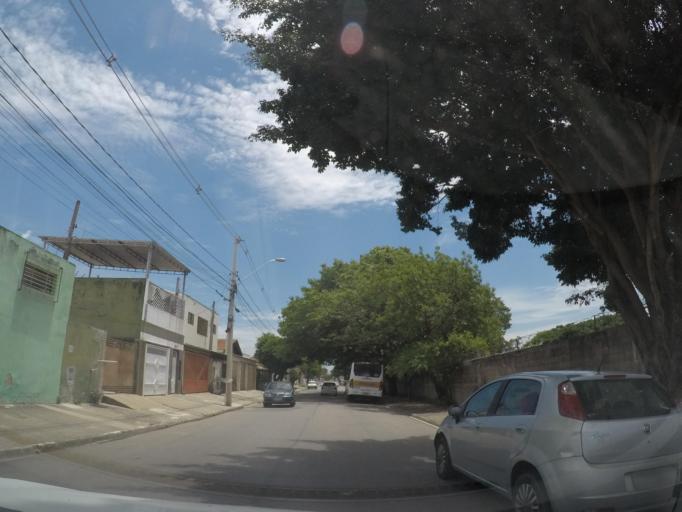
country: BR
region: Sao Paulo
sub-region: Hortolandia
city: Hortolandia
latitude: -22.8444
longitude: -47.1941
